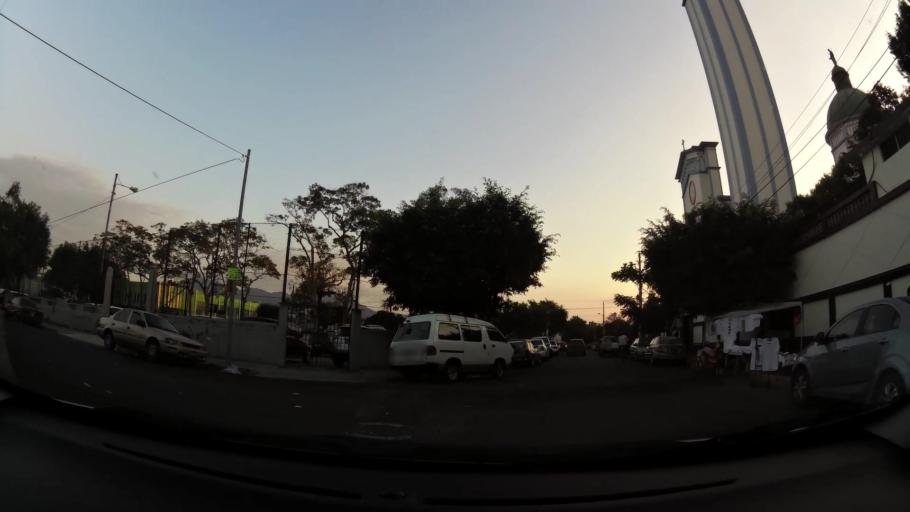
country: SV
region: San Salvador
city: San Salvador
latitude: 13.7117
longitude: -89.1920
